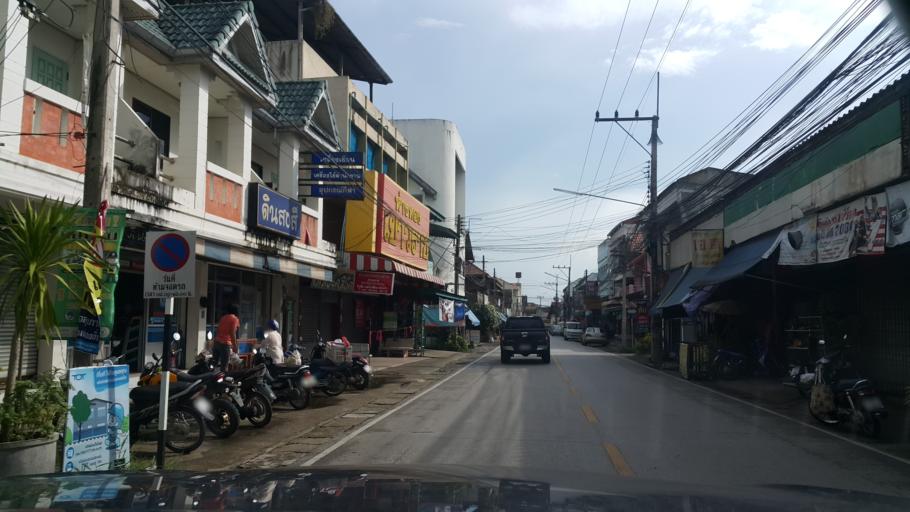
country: TH
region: Lampang
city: Thoen
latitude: 17.6044
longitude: 99.2092
